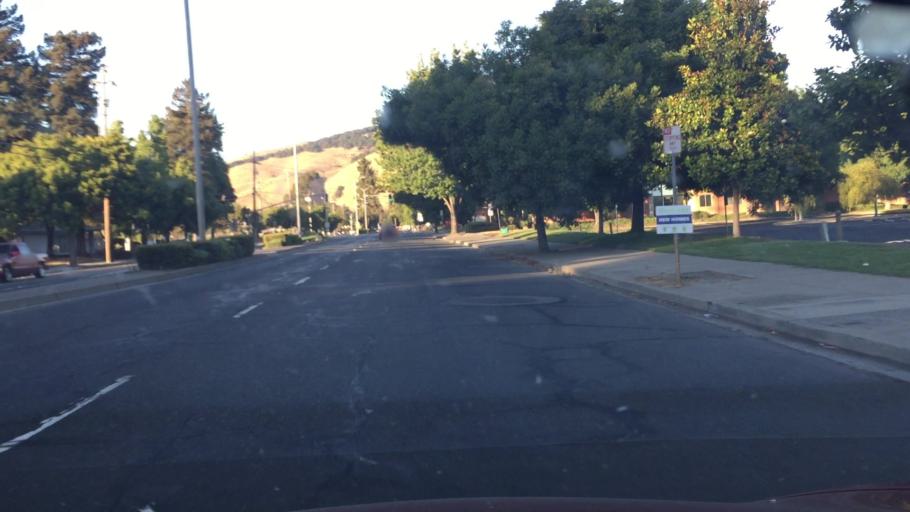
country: US
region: California
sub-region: Alameda County
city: Fremont
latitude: 37.5668
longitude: -121.9741
